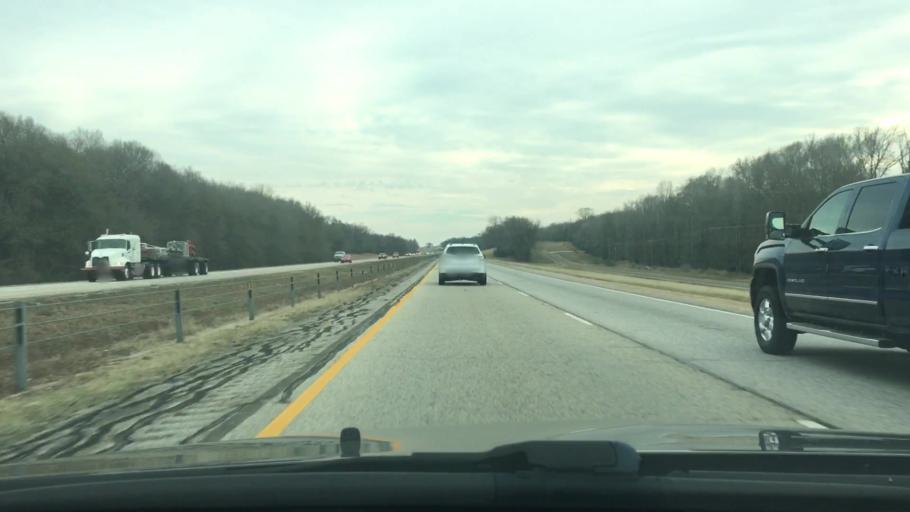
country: US
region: Texas
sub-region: Leon County
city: Centerville
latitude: 31.3062
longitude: -96.0015
